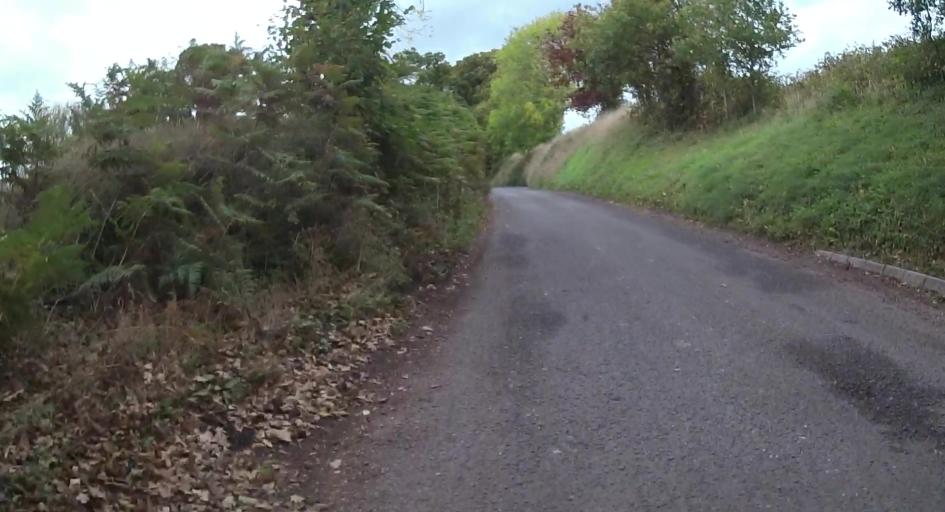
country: GB
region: England
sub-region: Hampshire
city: Alton
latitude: 51.1343
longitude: -0.9358
